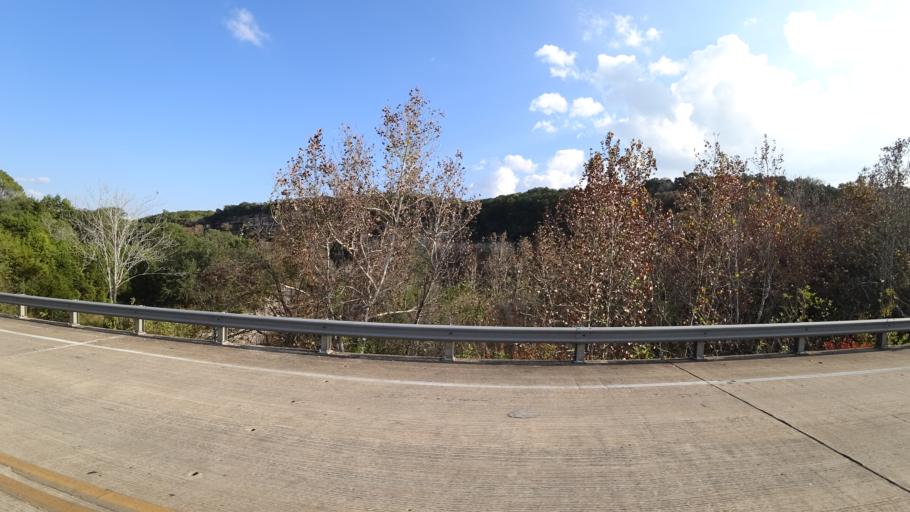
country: US
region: Texas
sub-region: Travis County
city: Lost Creek
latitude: 30.2741
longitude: -97.8444
